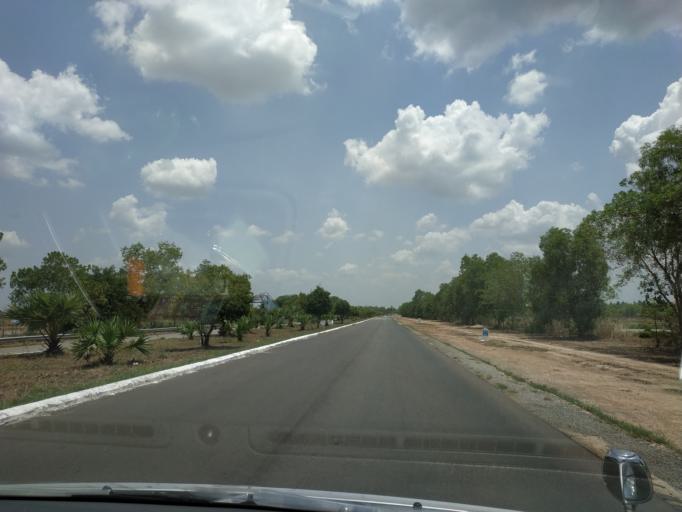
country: MM
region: Bago
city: Thanatpin
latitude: 17.0972
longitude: 96.1778
